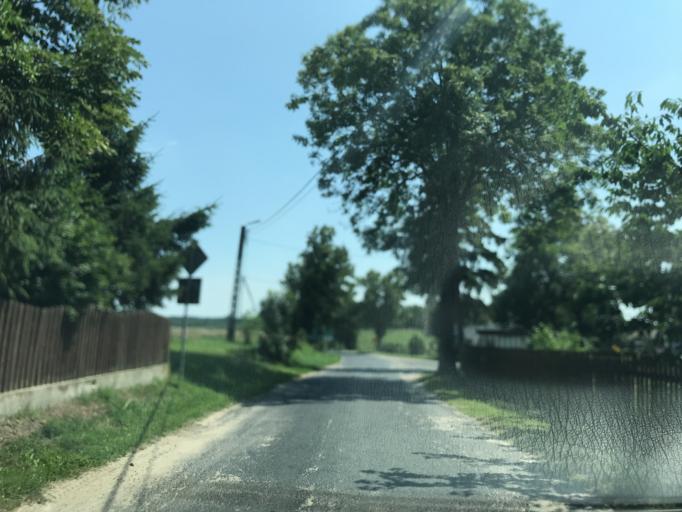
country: PL
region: Kujawsko-Pomorskie
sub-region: Powiat golubsko-dobrzynski
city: Zbojno
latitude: 52.9752
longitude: 19.1975
